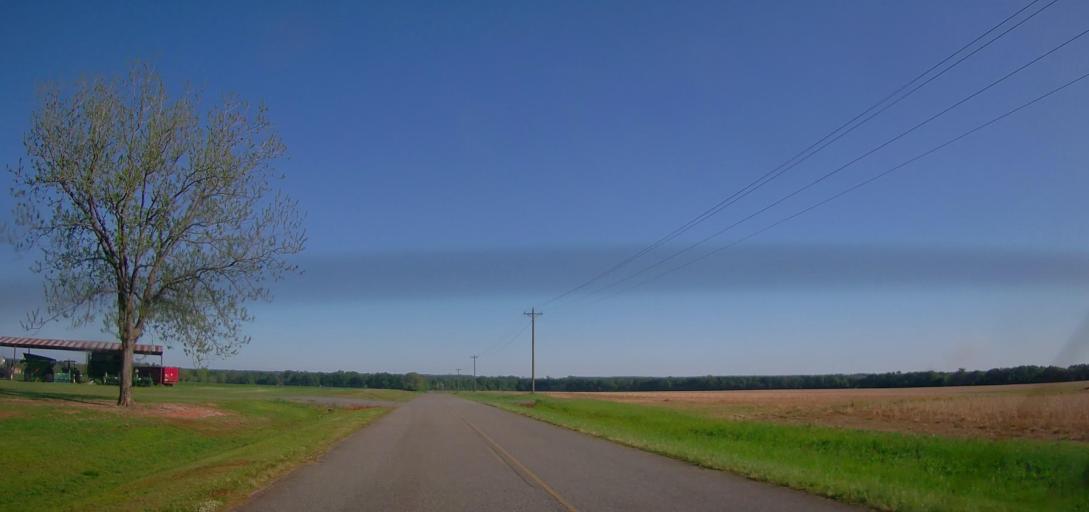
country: US
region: Georgia
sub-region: Houston County
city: Perry
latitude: 32.4288
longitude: -83.7813
